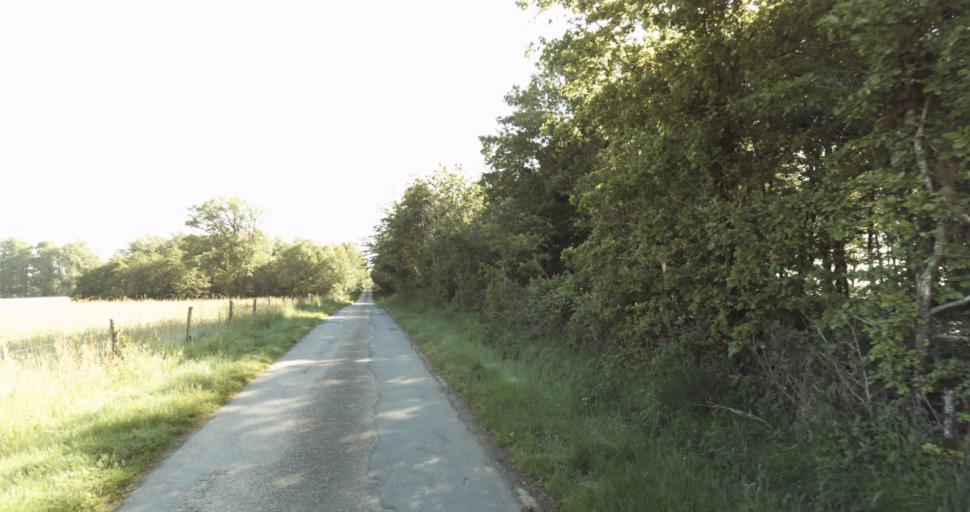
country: FR
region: Limousin
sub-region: Departement de la Haute-Vienne
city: Bosmie-l'Aiguille
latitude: 45.7187
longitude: 1.2290
